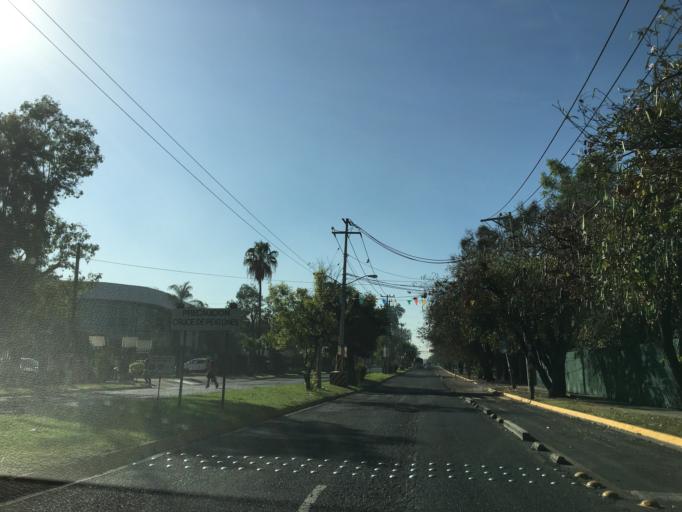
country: MX
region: Jalisco
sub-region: Tlajomulco de Zuniga
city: La Tijera
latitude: 20.6172
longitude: -103.4222
